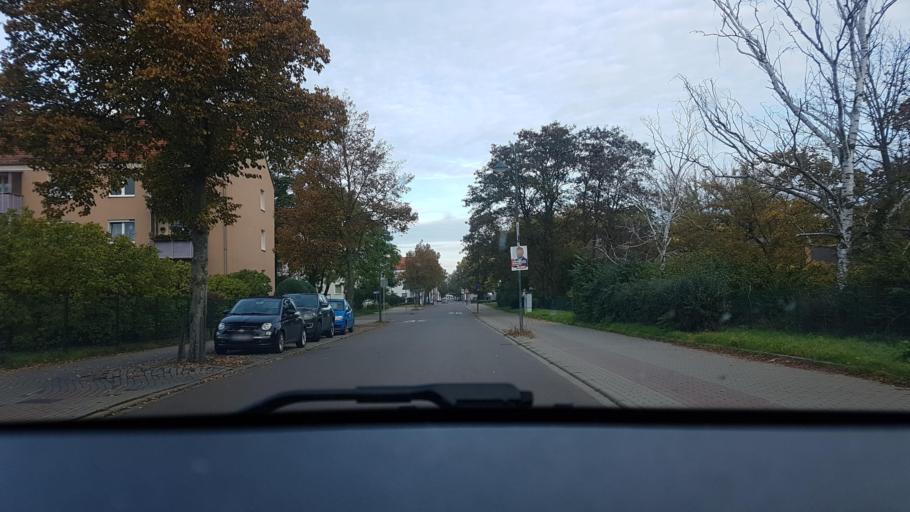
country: DE
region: Saxony-Anhalt
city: Bernburg
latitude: 51.7851
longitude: 11.7489
